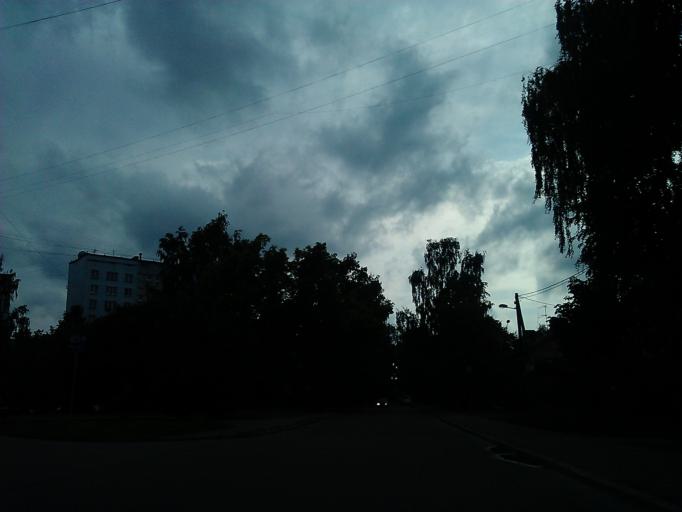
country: LV
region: Riga
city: Riga
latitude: 56.9576
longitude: 24.1696
